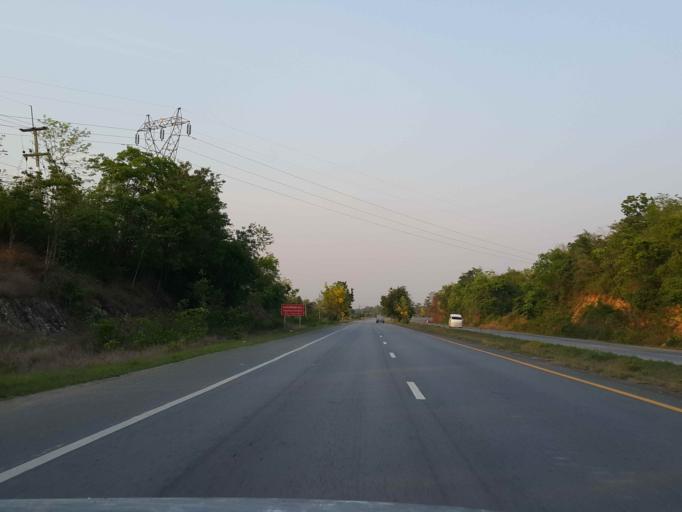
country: TH
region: Lampang
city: Sop Prap
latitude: 17.8564
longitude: 99.3056
